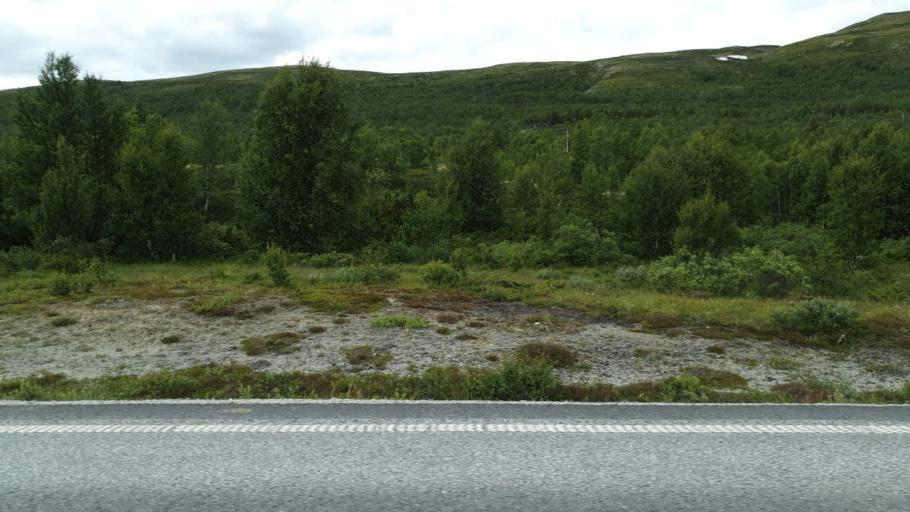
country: NO
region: Oppland
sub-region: Dovre
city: Dovre
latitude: 62.2007
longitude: 9.5383
